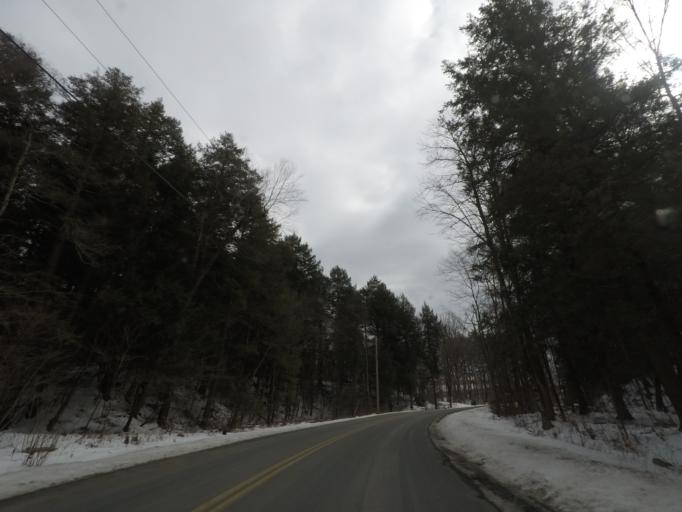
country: US
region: New York
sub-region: Rensselaer County
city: Hoosick Falls
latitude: 42.8799
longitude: -73.4131
